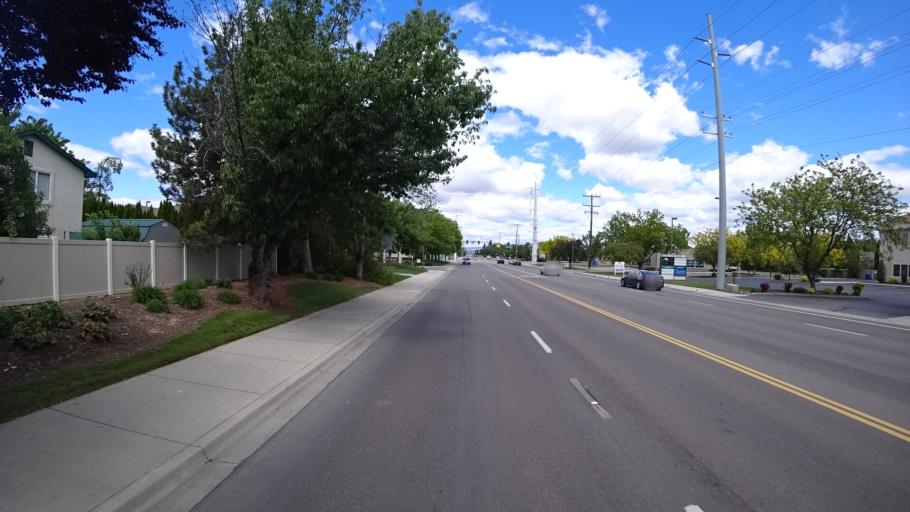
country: US
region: Idaho
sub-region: Ada County
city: Eagle
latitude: 43.6474
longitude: -116.3344
